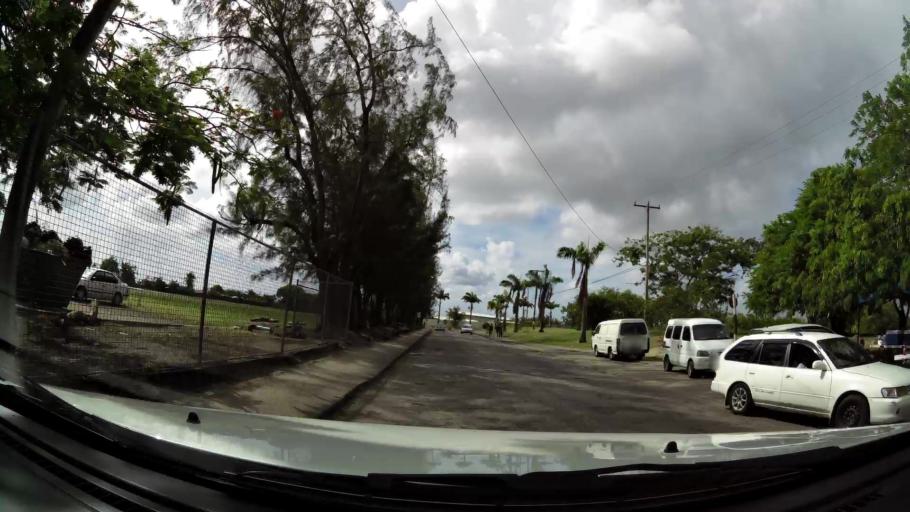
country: BB
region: Saint Michael
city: Bridgetown
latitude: 13.1179
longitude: -59.6021
